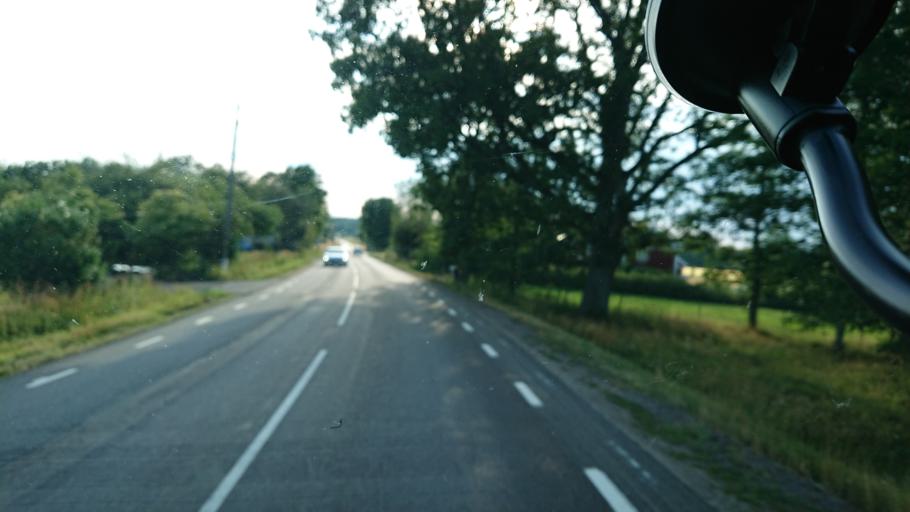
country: SE
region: Kronoberg
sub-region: Vaxjo Kommun
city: Braas
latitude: 57.0227
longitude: 15.0299
